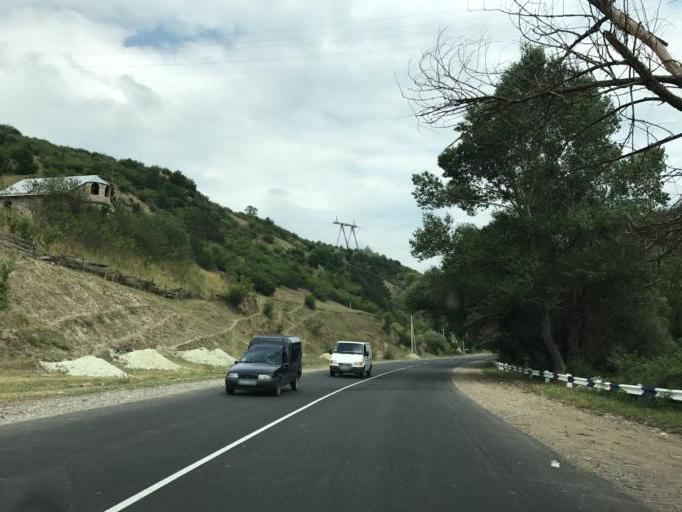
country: AM
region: Tavush
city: Haghartsin
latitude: 40.7736
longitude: 44.9859
